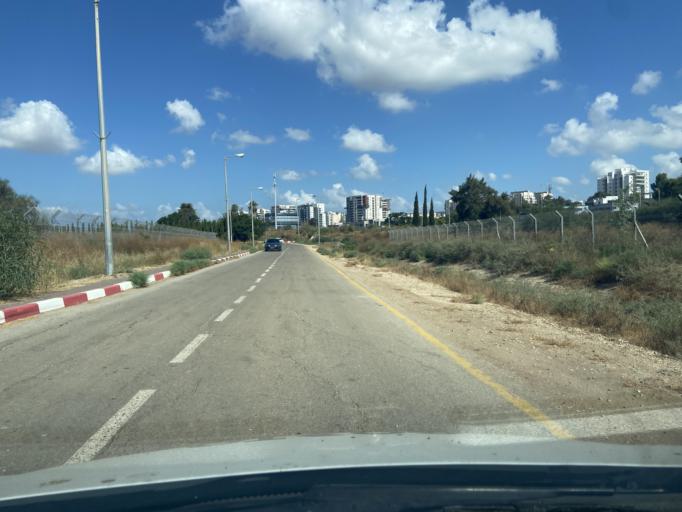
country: IL
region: Central District
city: Yehud
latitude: 32.0246
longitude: 34.8949
